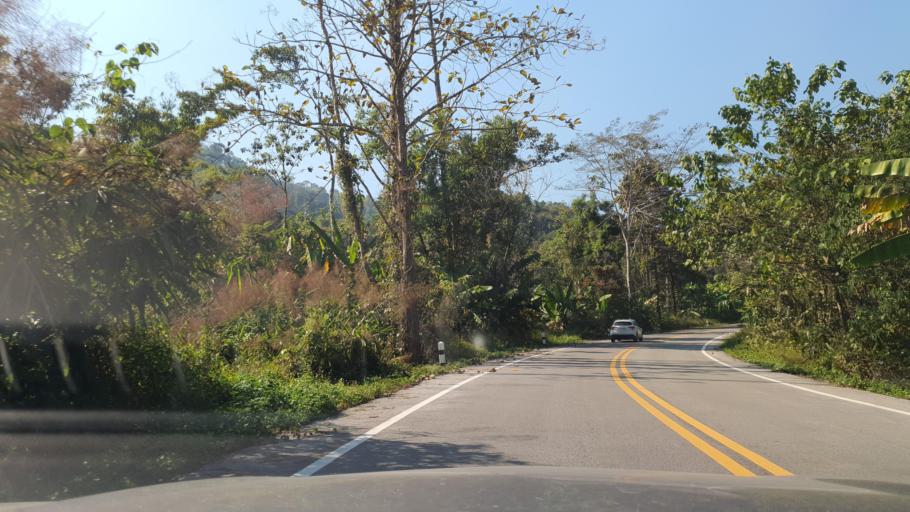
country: TH
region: Chiang Rai
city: Mae Lao
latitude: 19.8696
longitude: 99.6325
